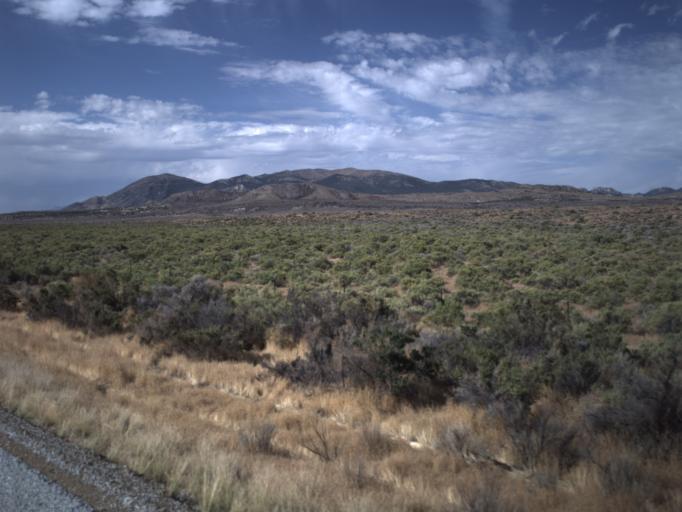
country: US
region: Utah
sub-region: Tooele County
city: Wendover
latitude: 41.5577
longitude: -113.5843
